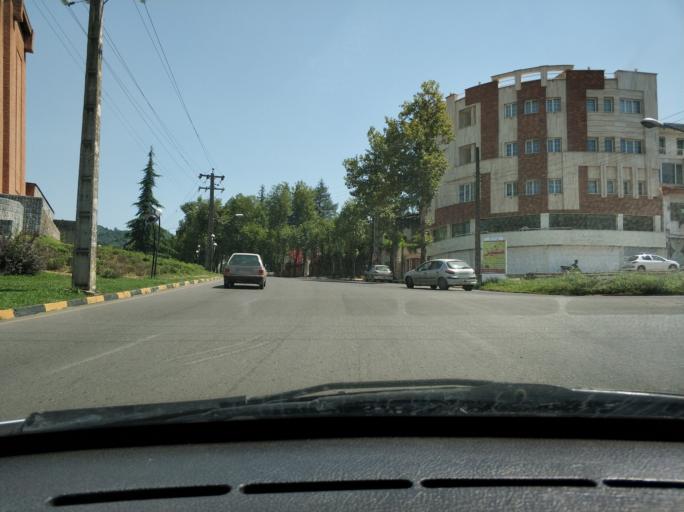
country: IR
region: Gilan
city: Lahijan
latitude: 37.1963
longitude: 50.0155
